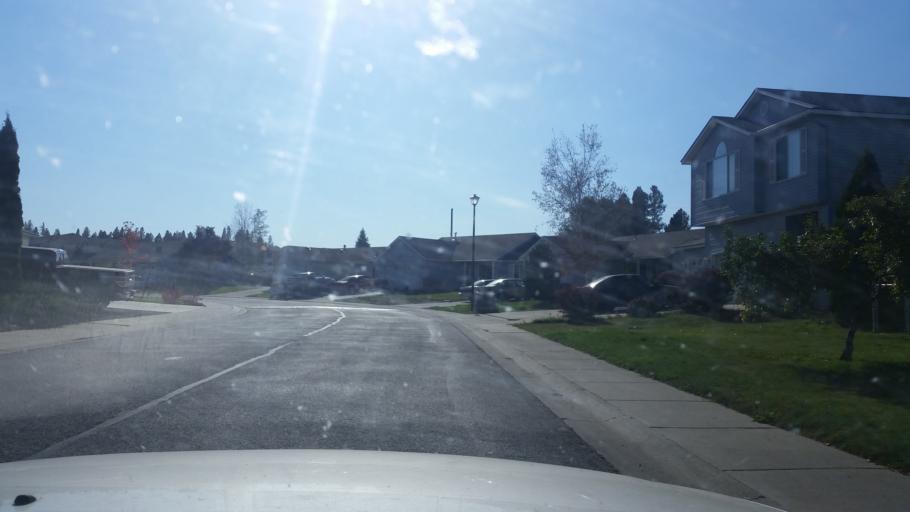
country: US
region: Washington
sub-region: Spokane County
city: Cheney
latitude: 47.5098
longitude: -117.5665
